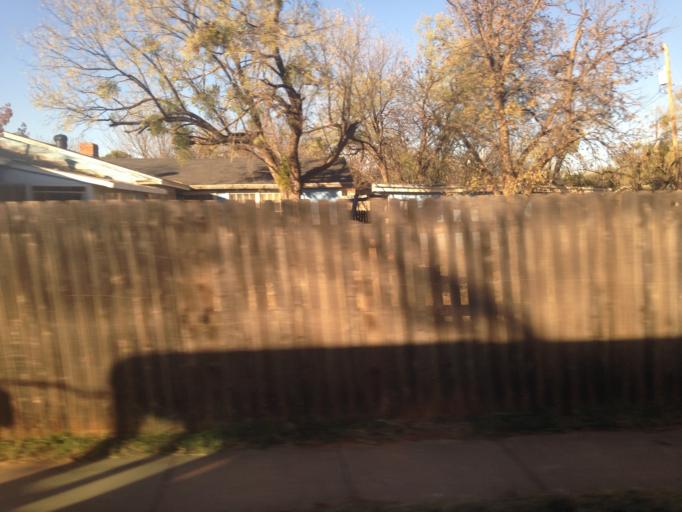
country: US
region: Texas
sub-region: Taylor County
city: Abilene
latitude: 32.4439
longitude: -99.7748
